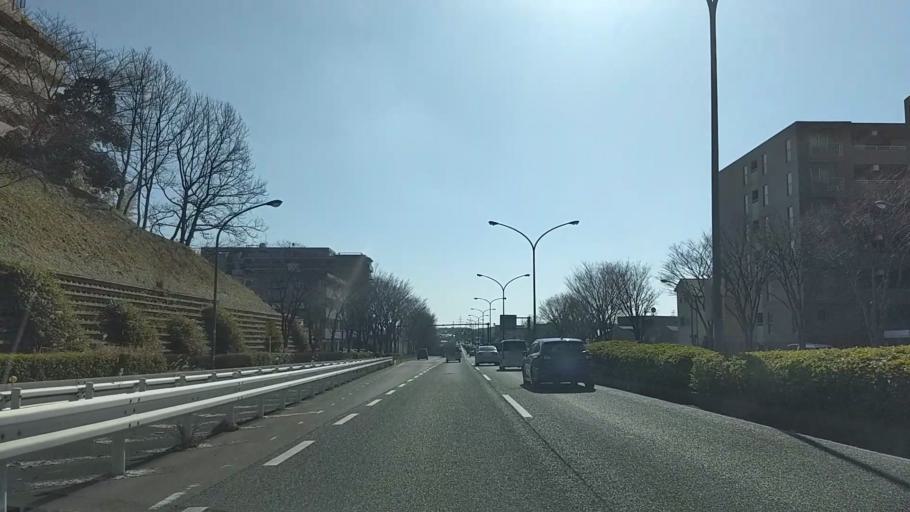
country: JP
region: Kanagawa
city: Yokohama
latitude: 35.4240
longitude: 139.5610
